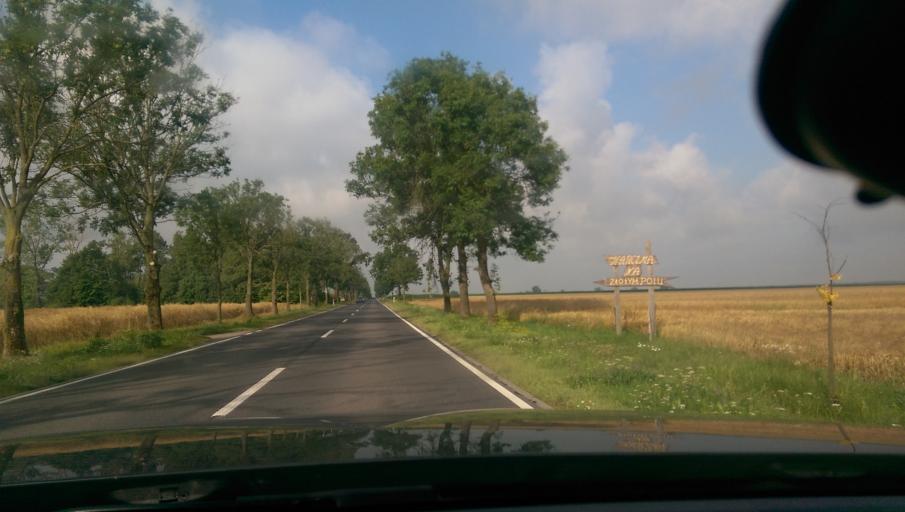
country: PL
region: Masovian Voivodeship
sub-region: Powiat przasnyski
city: Przasnysz
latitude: 52.9735
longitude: 20.8019
